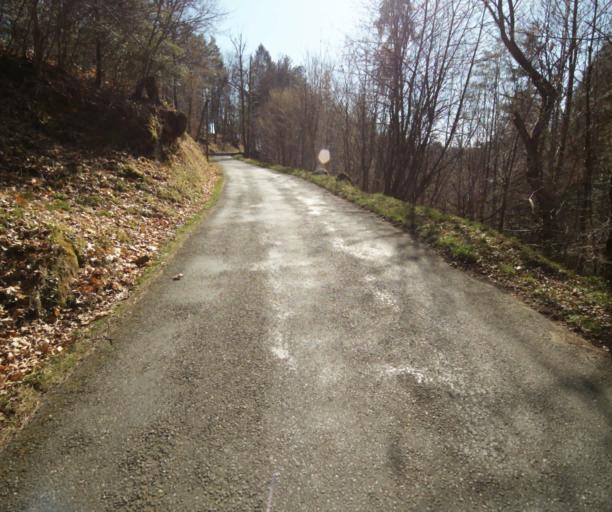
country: FR
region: Limousin
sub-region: Departement de la Correze
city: Tulle
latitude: 45.2817
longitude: 1.7362
